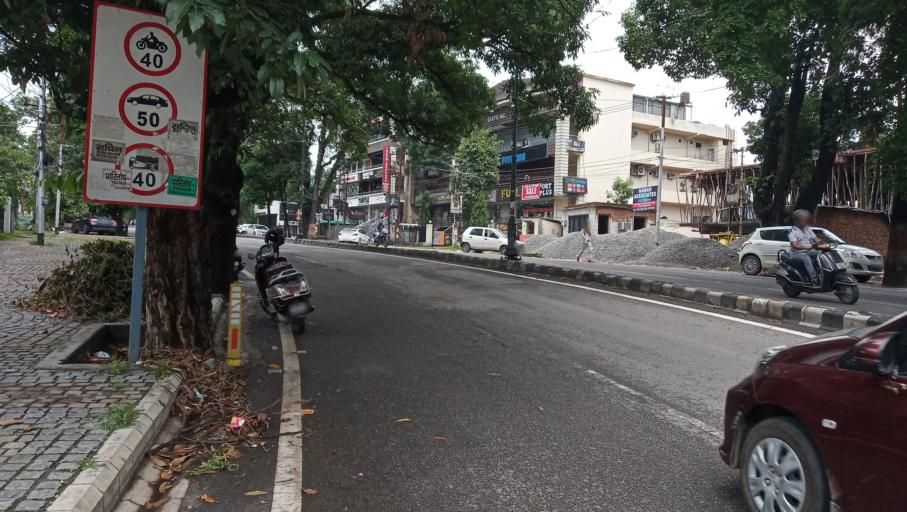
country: IN
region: Uttarakhand
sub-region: Dehradun
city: Dehradun
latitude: 30.3686
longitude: 78.0739
